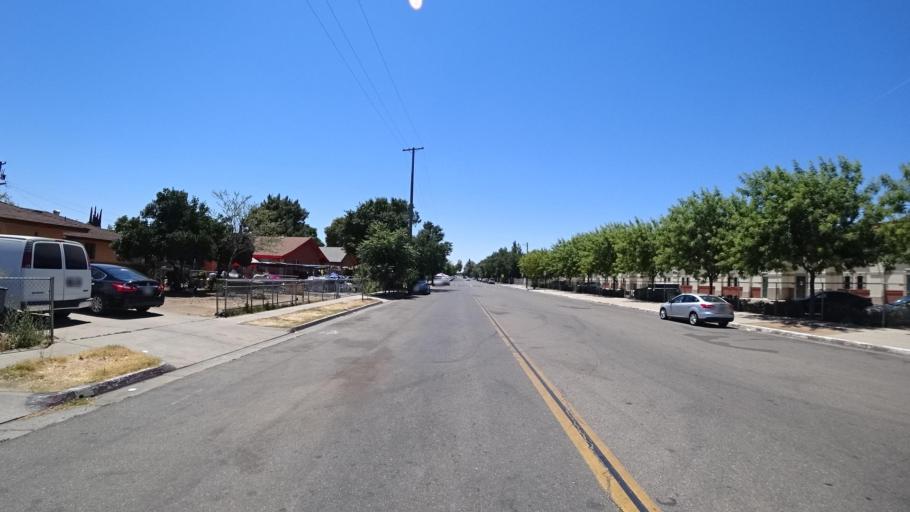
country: US
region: California
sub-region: Fresno County
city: Fresno
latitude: 36.7425
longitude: -119.7500
